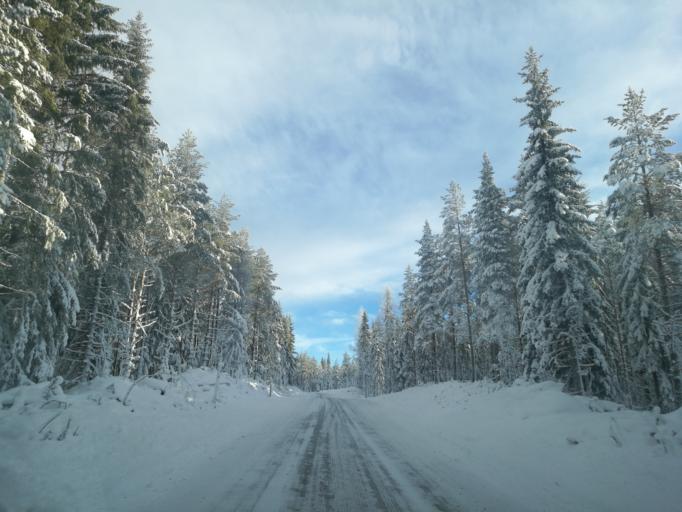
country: SE
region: Vaermland
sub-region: Torsby Kommun
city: Torsby
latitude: 60.6601
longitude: 12.8204
